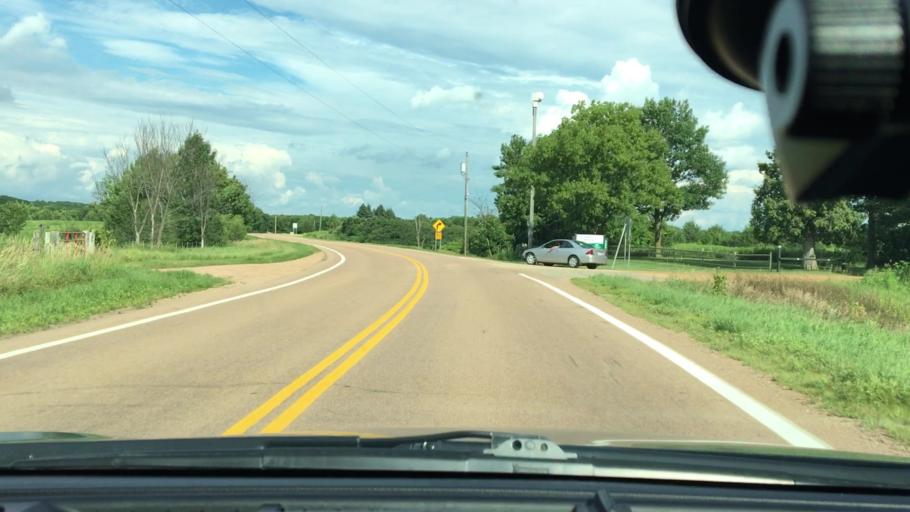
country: US
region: Minnesota
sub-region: Carver County
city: Victoria
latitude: 44.8723
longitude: -93.6851
